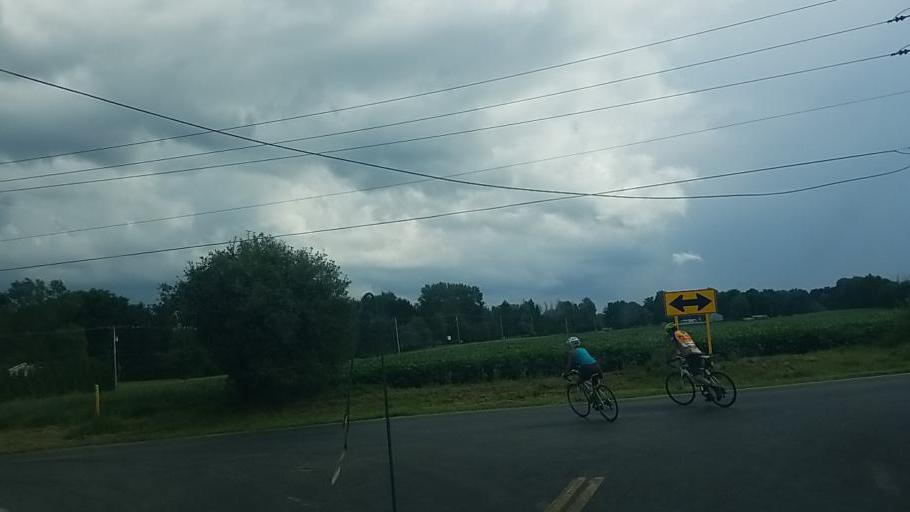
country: US
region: Ohio
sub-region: Wayne County
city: Creston
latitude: 41.0032
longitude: -81.9111
